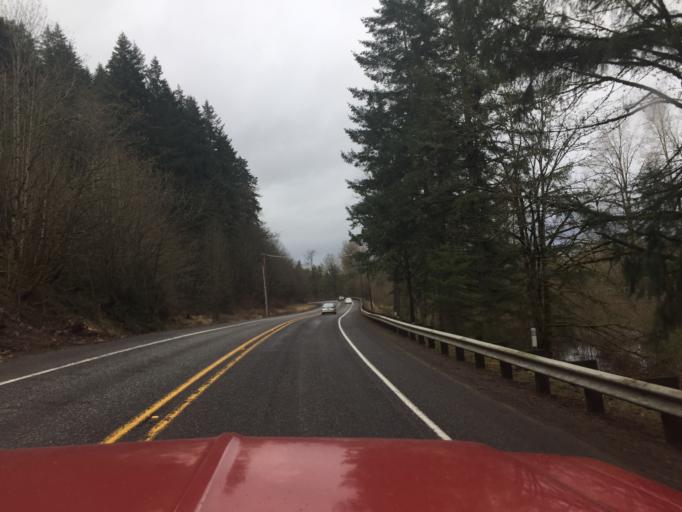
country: US
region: Washington
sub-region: Cowlitz County
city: Kalama
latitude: 46.0244
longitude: -122.8824
